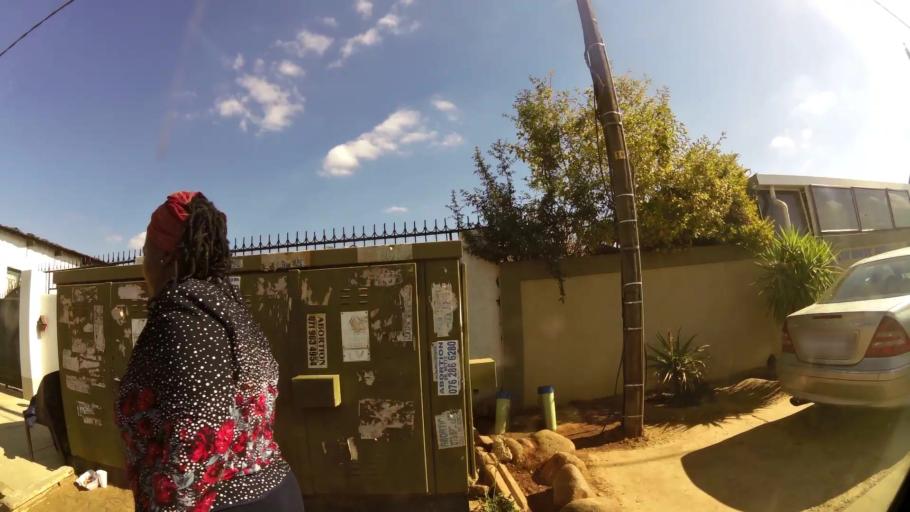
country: ZA
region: Gauteng
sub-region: City of Tshwane Metropolitan Municipality
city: Cullinan
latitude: -25.7165
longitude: 28.4087
